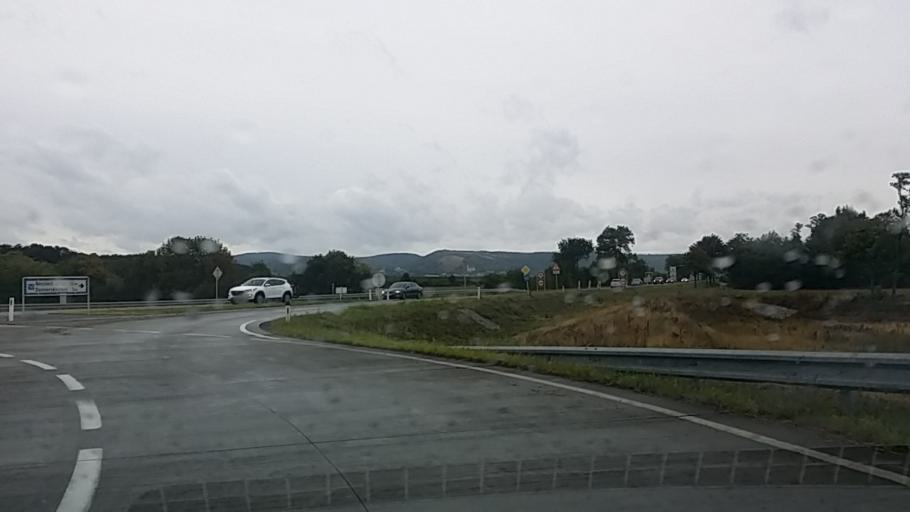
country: AT
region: Burgenland
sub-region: Eisenstadt-Umgebung
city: Donnerskirchen
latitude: 47.8686
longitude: 16.6475
